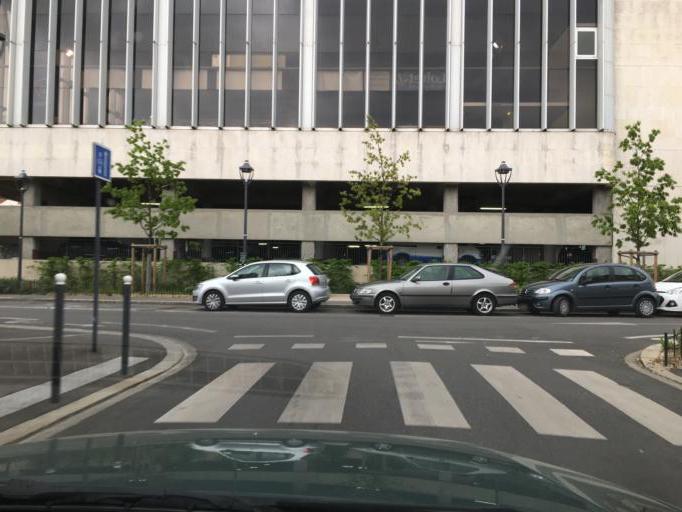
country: FR
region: Centre
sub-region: Departement du Loiret
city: Orleans
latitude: 47.9033
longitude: 1.8920
